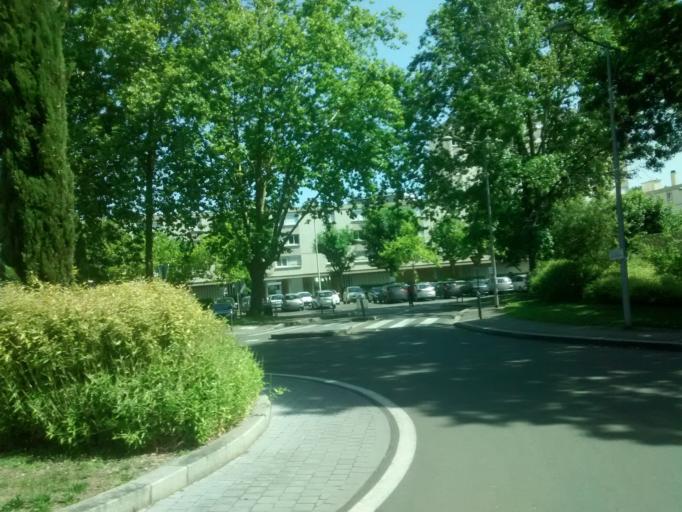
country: FR
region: Aquitaine
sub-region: Departement de la Gironde
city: Merignac
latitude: 44.8413
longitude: -0.6509
